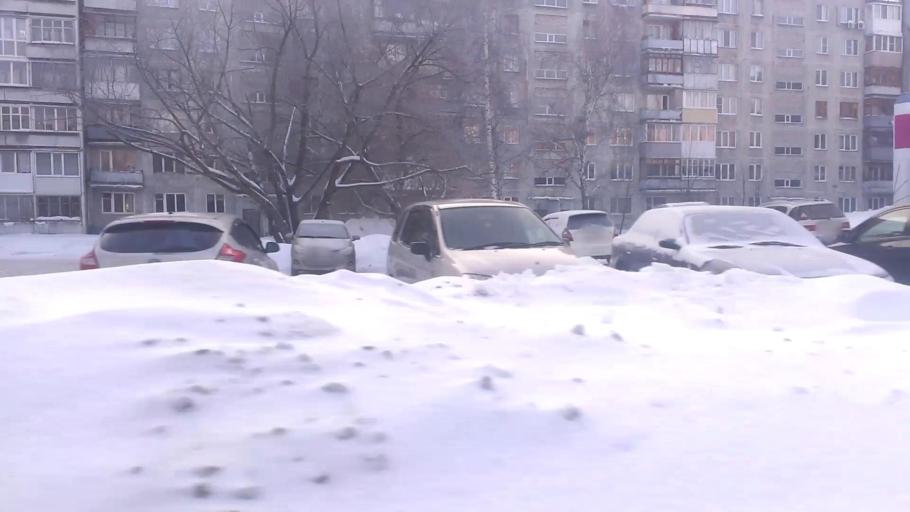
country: RU
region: Altai Krai
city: Novosilikatnyy
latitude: 53.3740
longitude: 83.6669
